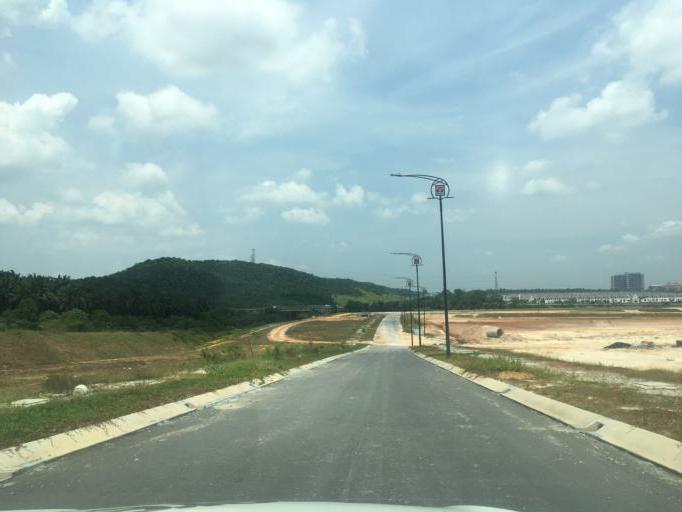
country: MY
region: Putrajaya
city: Putrajaya
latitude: 2.8477
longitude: 101.7105
